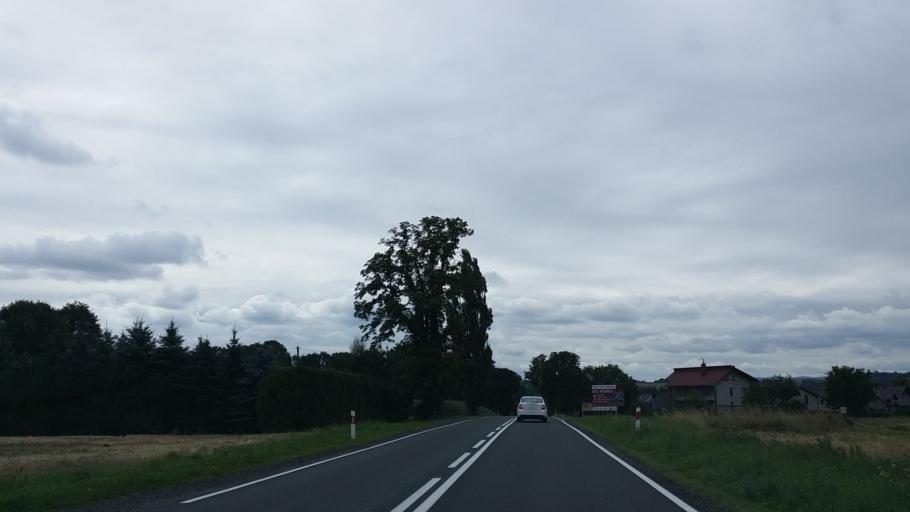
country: PL
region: Lesser Poland Voivodeship
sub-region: Powiat wadowicki
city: Radocza
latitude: 49.9508
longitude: 19.4465
